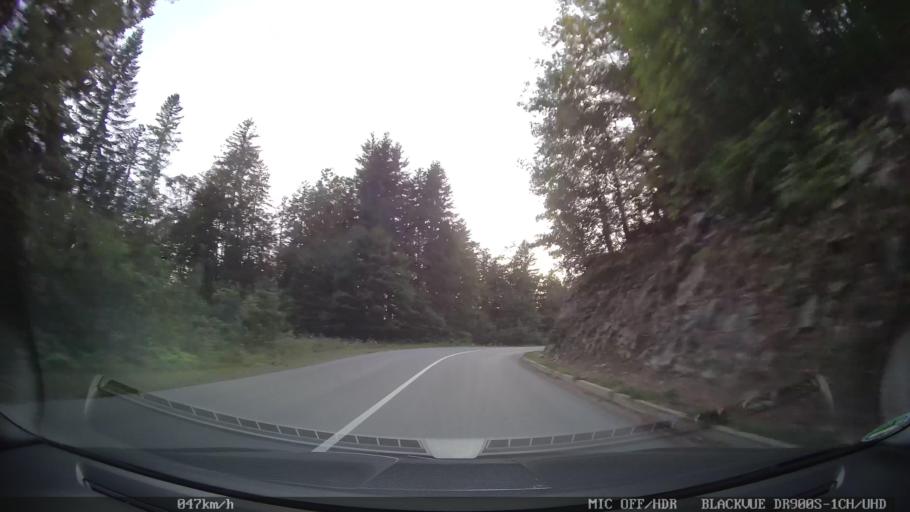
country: HR
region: Primorsko-Goranska
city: Novi Vinodolski
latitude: 45.1841
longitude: 14.9263
